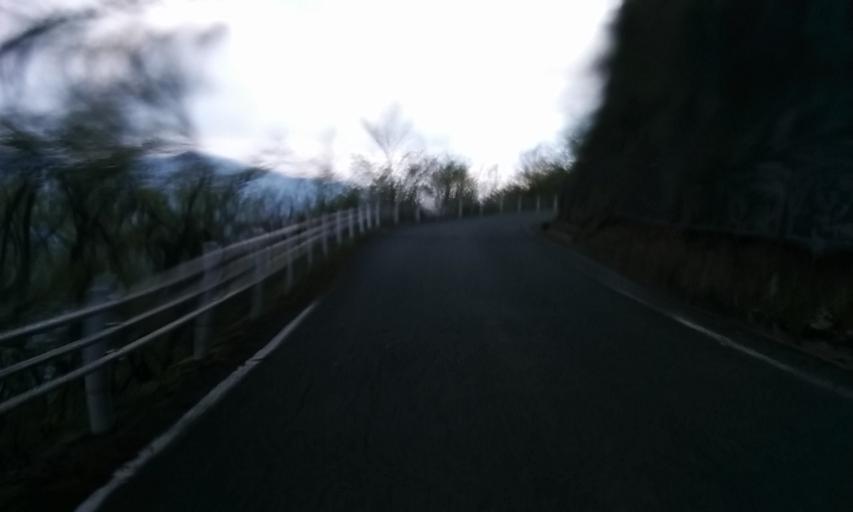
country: JP
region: Ehime
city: Saijo
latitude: 33.7914
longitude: 133.2776
